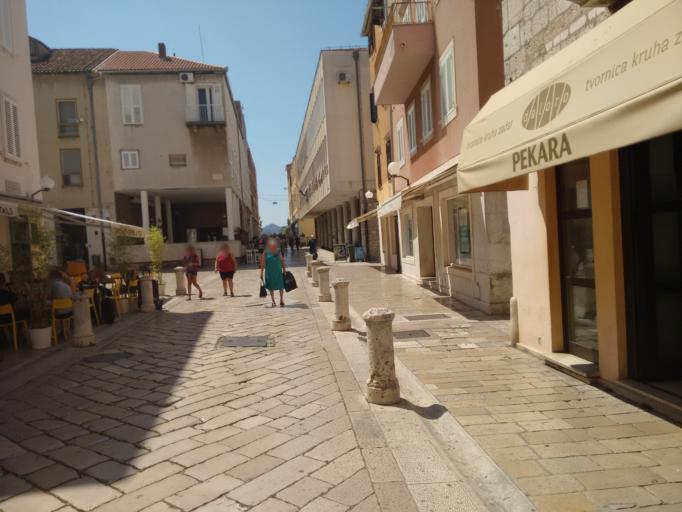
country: HR
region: Zadarska
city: Zadar
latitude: 44.1165
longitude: 15.2263
